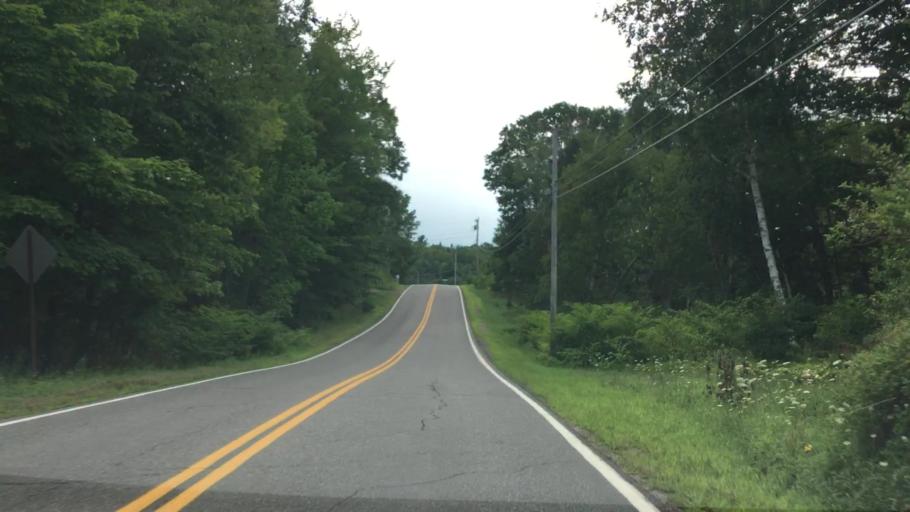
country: US
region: Maine
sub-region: Waldo County
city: Lincolnville
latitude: 44.3157
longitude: -69.0843
